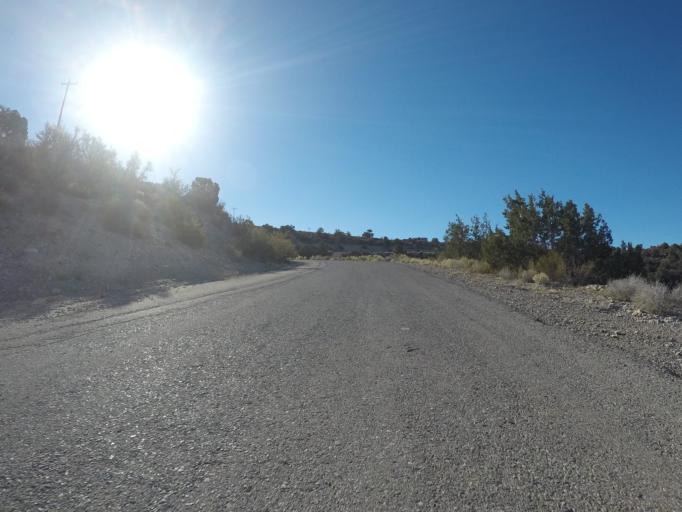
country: US
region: Nevada
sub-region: Clark County
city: Summerlin South
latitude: 36.0834
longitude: -115.5598
